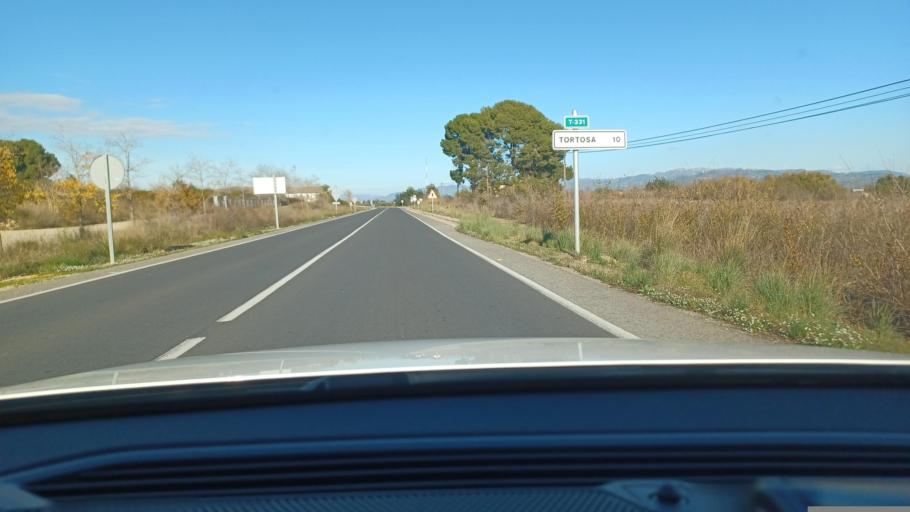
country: ES
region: Catalonia
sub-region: Provincia de Tarragona
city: Santa Barbara
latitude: 40.7239
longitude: 0.5031
